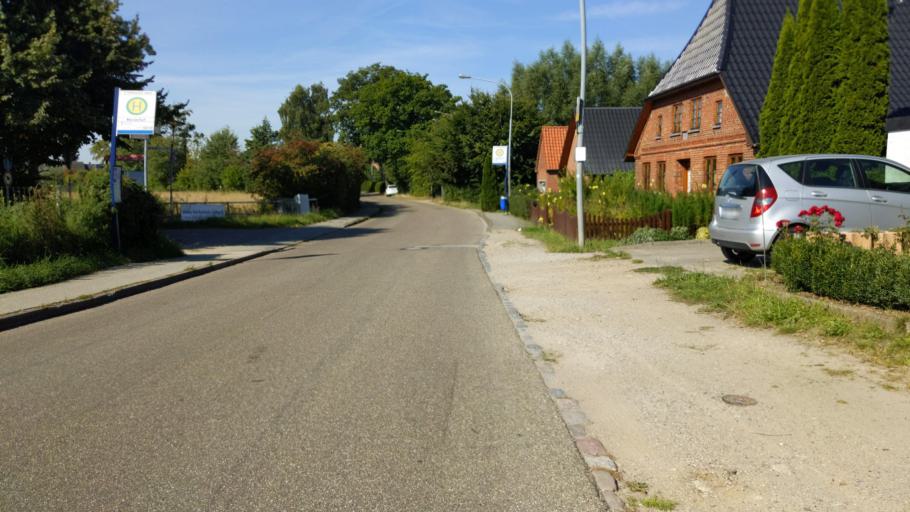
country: DE
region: Schleswig-Holstein
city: Stockelsdorf
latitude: 53.8830
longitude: 10.6331
